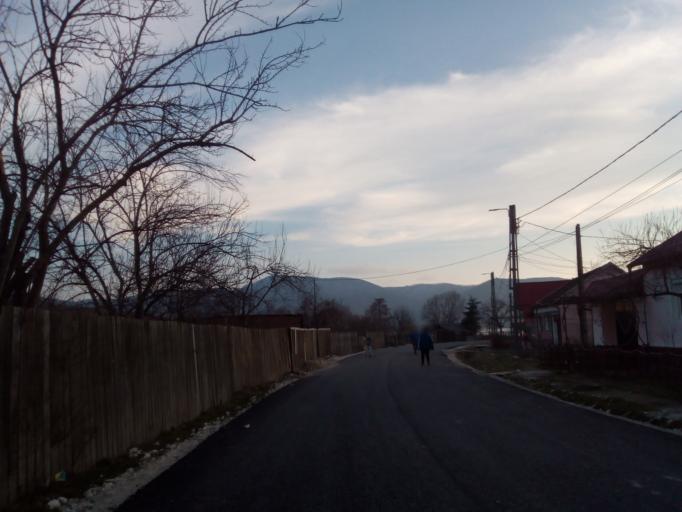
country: RO
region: Mehedinti
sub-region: Comuna Eselnita
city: Eselnita
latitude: 44.6945
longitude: 22.3665
